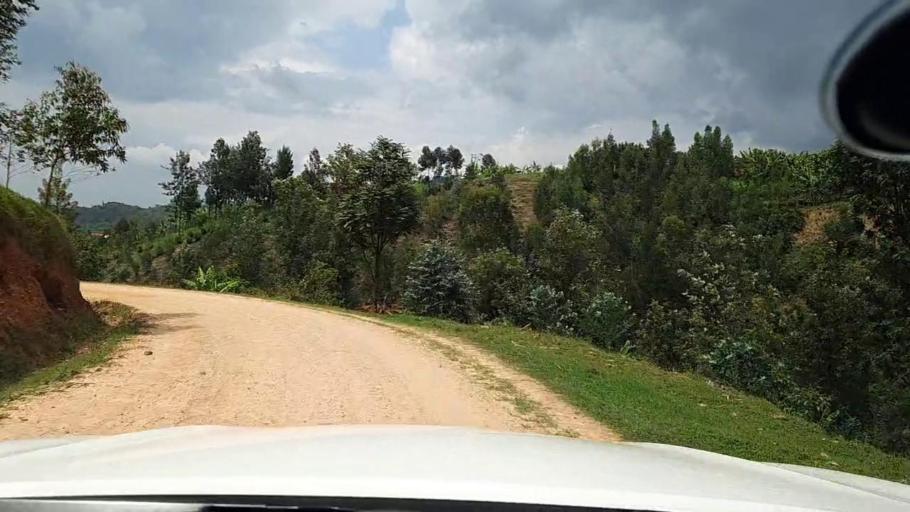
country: RW
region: Western Province
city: Kibuye
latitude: -2.1187
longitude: 29.4247
